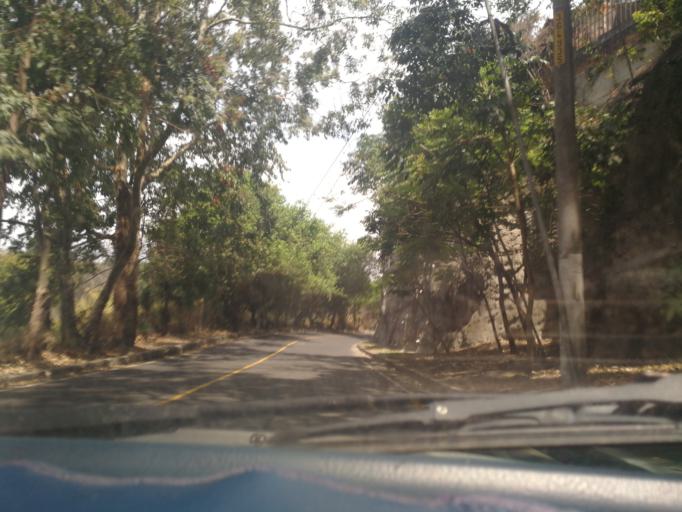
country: GT
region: Guatemala
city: Guatemala City
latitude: 14.6241
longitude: -90.4818
